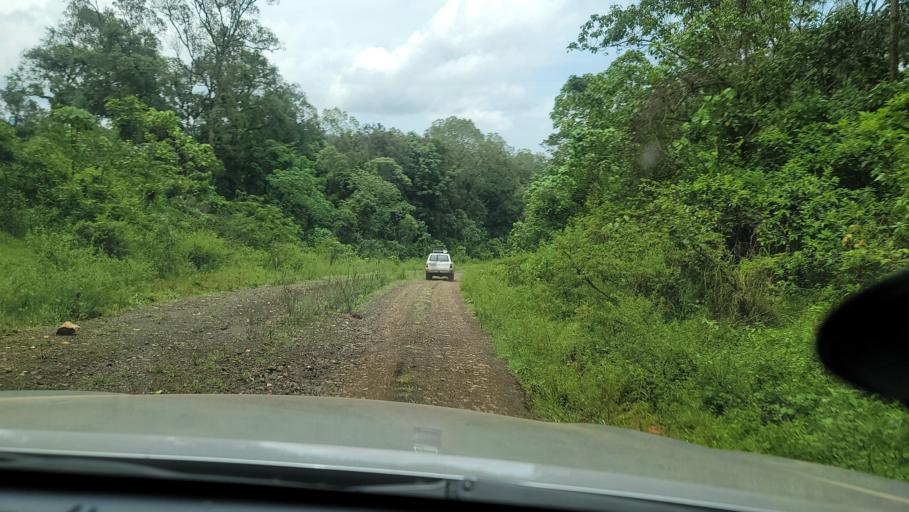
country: ET
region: Southern Nations, Nationalities, and People's Region
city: Bonga
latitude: 7.6618
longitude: 36.2466
